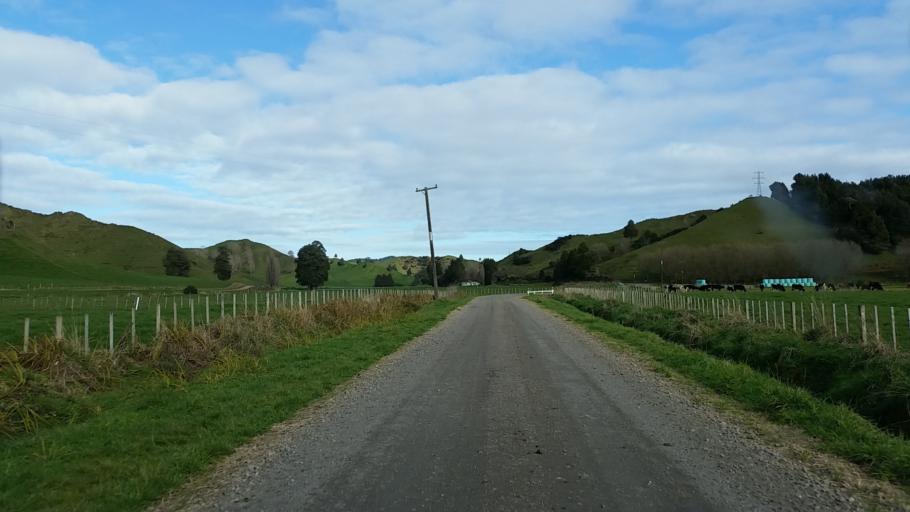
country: NZ
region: Taranaki
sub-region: South Taranaki District
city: Eltham
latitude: -39.2503
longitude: 174.5382
